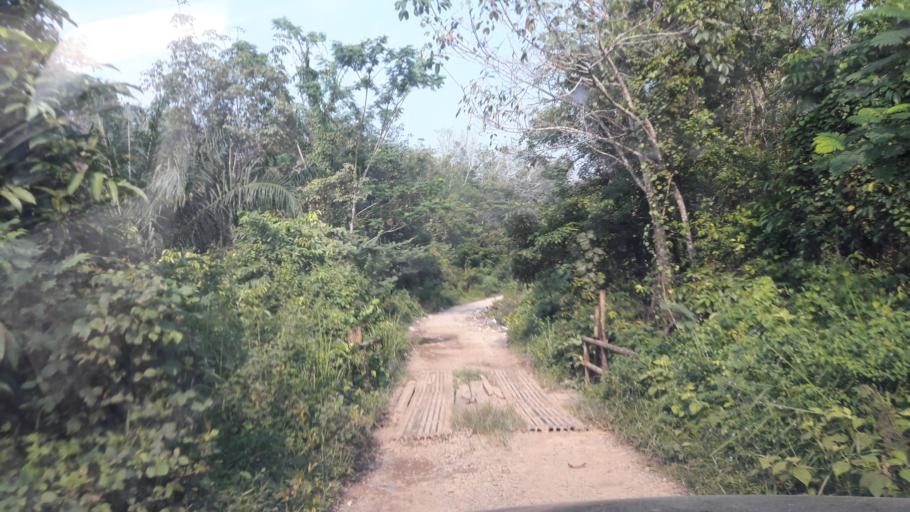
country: ID
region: South Sumatra
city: Gunungmegang Dalam
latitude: -3.2919
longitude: 103.8133
